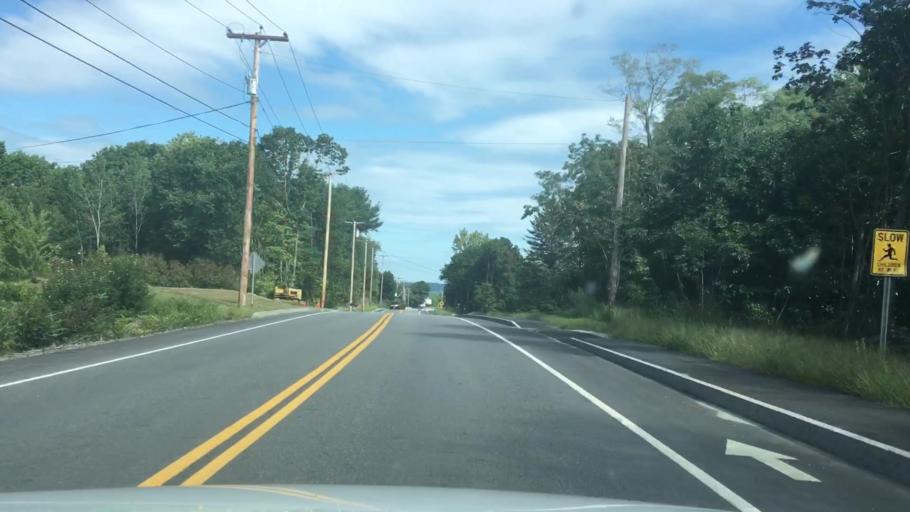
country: US
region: Maine
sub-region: Androscoggin County
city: Auburn
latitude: 44.1174
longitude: -70.2501
